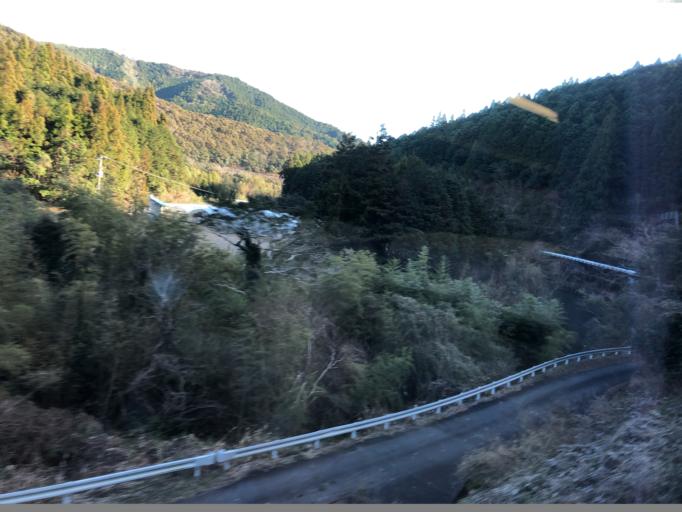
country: JP
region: Kochi
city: Nakamura
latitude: 33.1283
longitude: 133.1164
